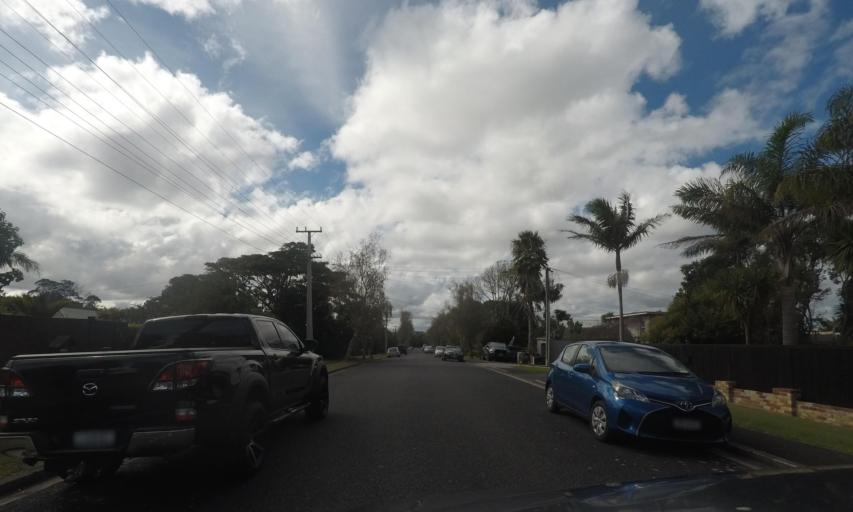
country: NZ
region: Auckland
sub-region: Auckland
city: Rosebank
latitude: -36.7814
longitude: 174.6442
